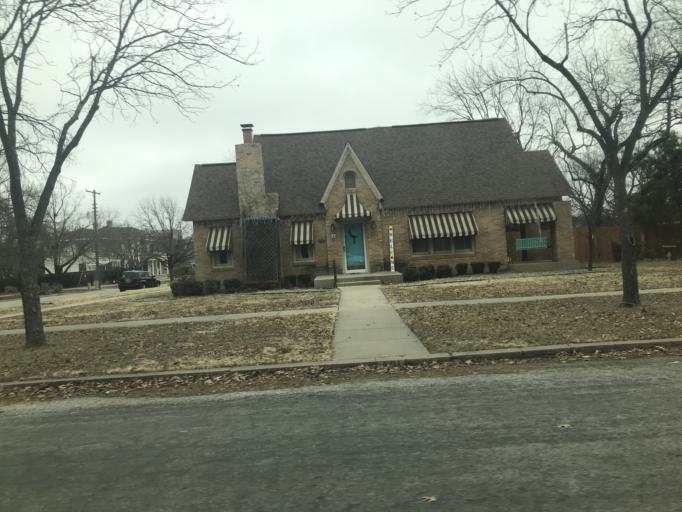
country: US
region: Texas
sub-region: Taylor County
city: Abilene
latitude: 32.4413
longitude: -99.7467
